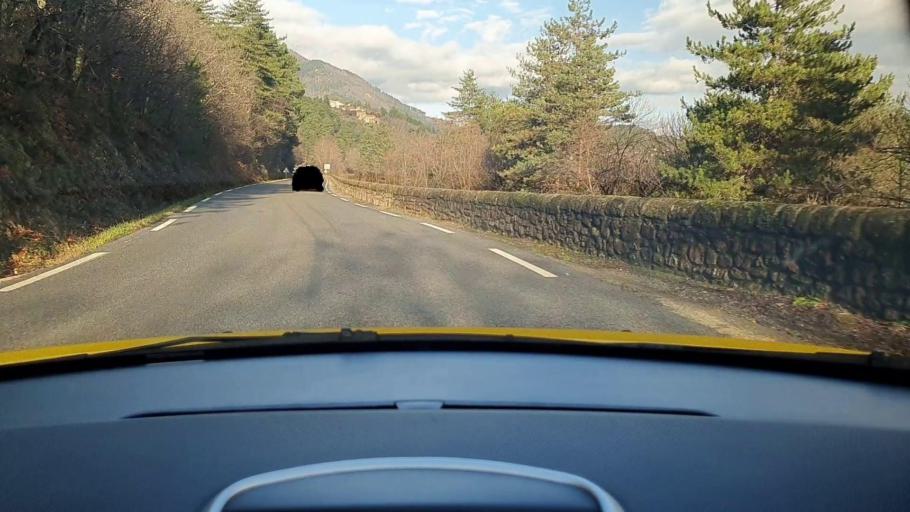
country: FR
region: Languedoc-Roussillon
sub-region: Departement du Gard
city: Branoux-les-Taillades
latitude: 44.3354
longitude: 3.9552
